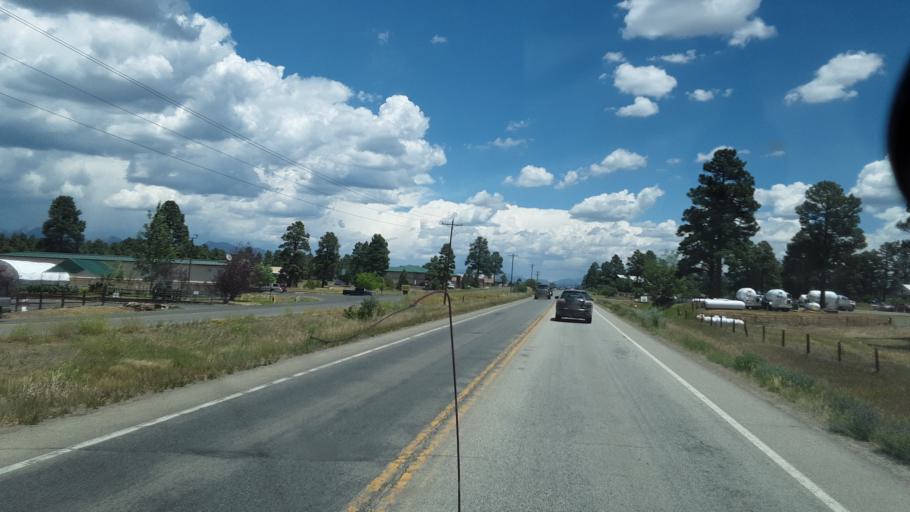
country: US
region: Colorado
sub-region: Archuleta County
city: Pagosa Springs
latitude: 37.2501
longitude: -107.0853
